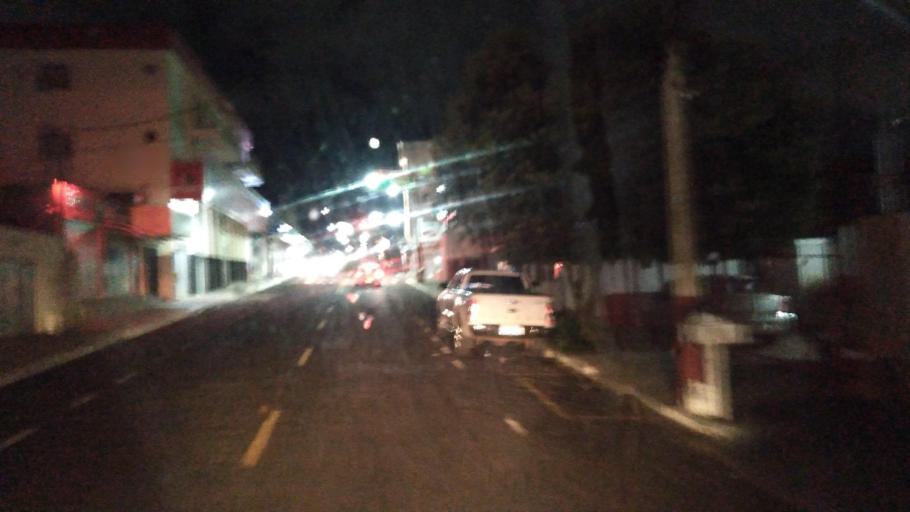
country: BR
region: Goias
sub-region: Mineiros
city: Mineiros
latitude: -17.5644
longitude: -52.5538
